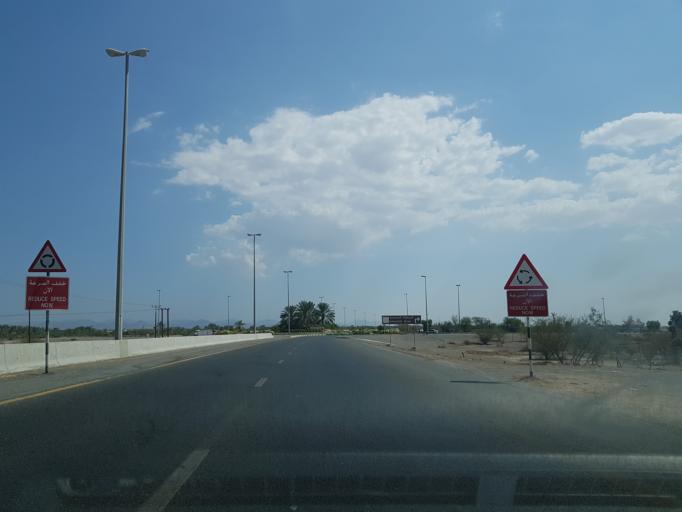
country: AE
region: Ash Shariqah
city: Adh Dhayd
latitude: 25.2441
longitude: 55.9129
